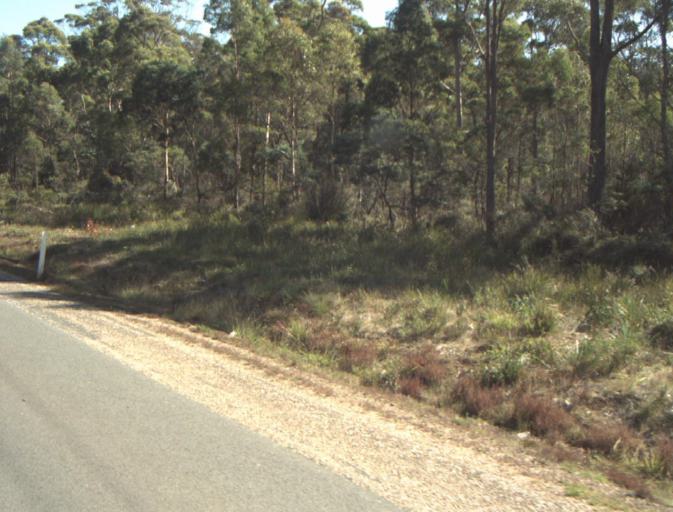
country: AU
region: Tasmania
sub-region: Launceston
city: Mayfield
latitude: -41.3172
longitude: 147.1925
